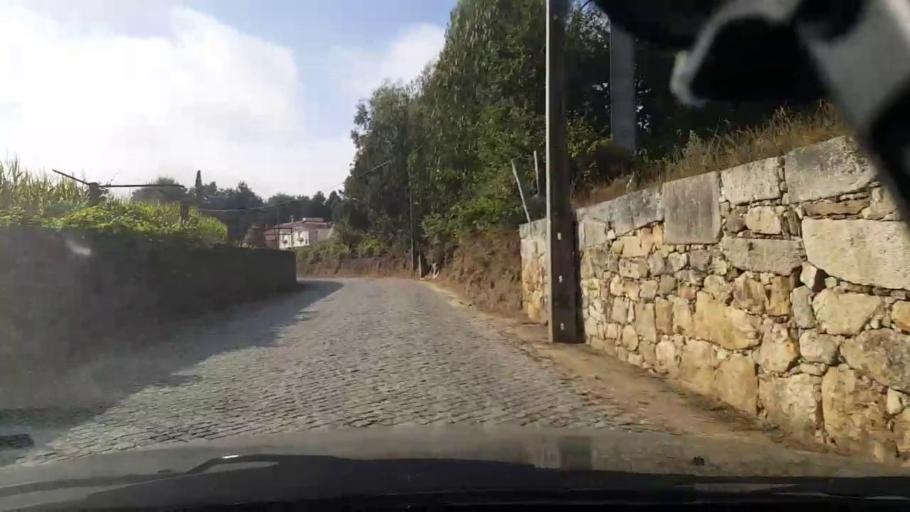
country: PT
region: Porto
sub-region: Maia
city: Gemunde
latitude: 41.2691
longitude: -8.6766
